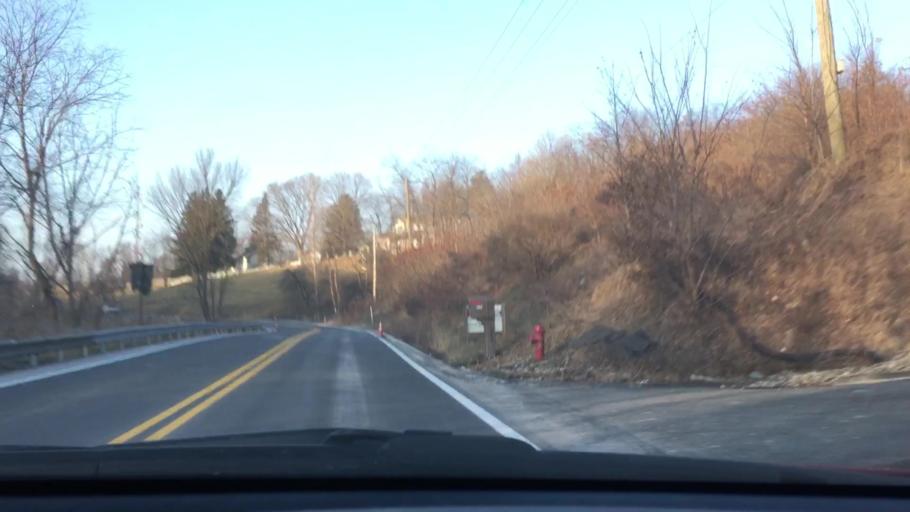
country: US
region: Pennsylvania
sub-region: Allegheny County
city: Oakdale
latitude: 40.4244
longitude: -80.2010
